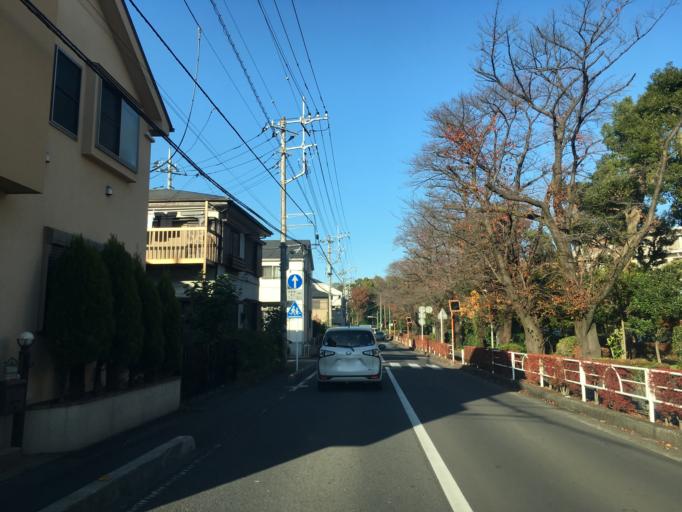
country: JP
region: Saitama
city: Tokorozawa
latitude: 35.8018
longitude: 139.4630
